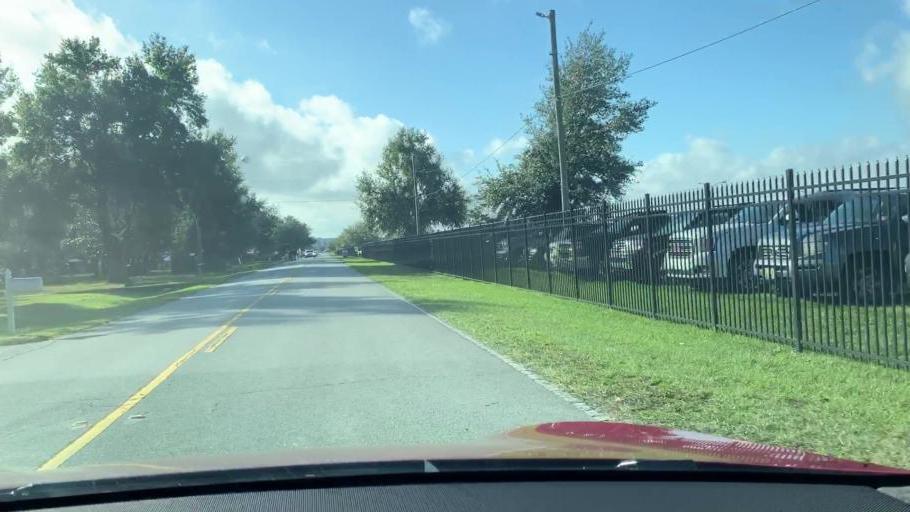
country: US
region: Florida
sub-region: Osceola County
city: Buenaventura Lakes
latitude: 28.3030
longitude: -81.3709
